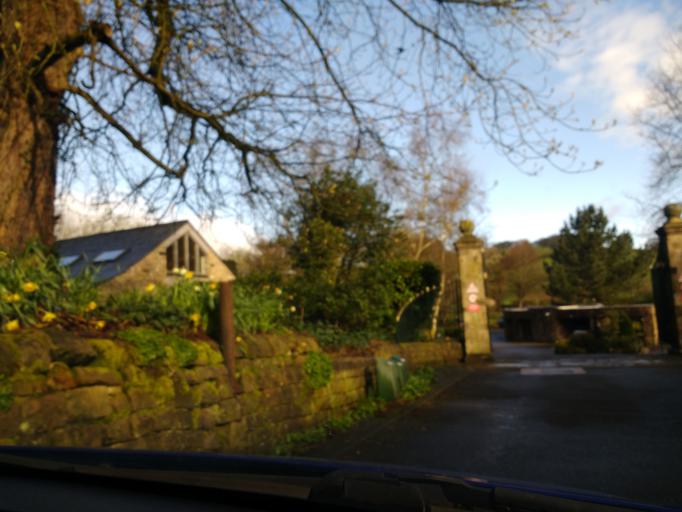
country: GB
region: England
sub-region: Lancashire
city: Caton
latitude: 54.0773
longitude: -2.7247
